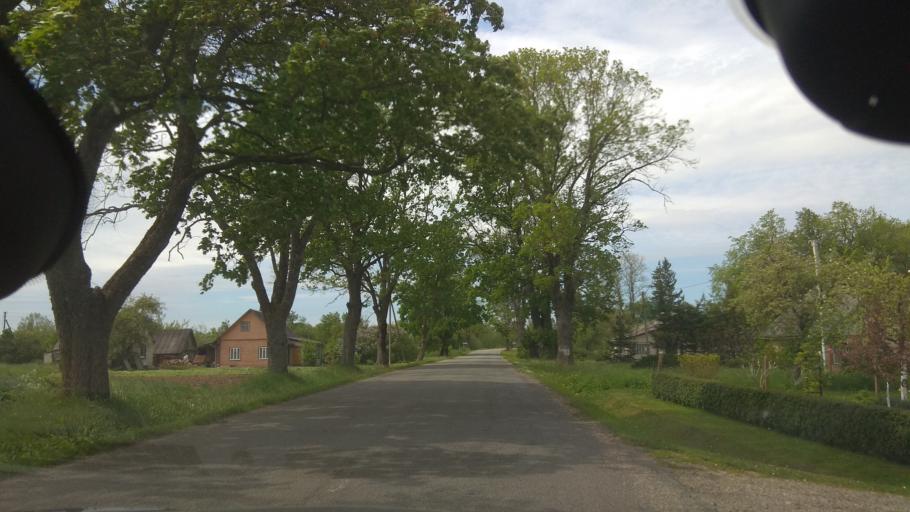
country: LT
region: Vilnius County
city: Ukmerge
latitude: 55.1485
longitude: 24.5638
